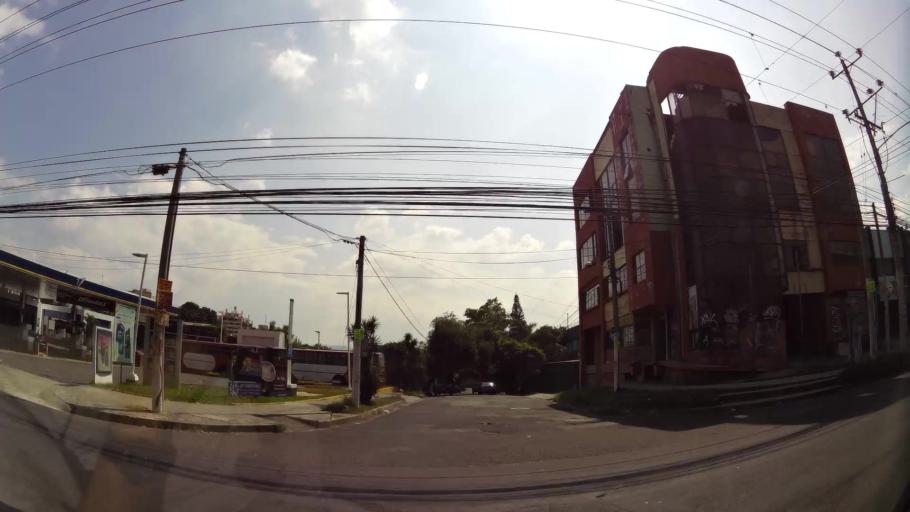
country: SV
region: San Salvador
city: Mejicanos
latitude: 13.7145
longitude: -89.2091
